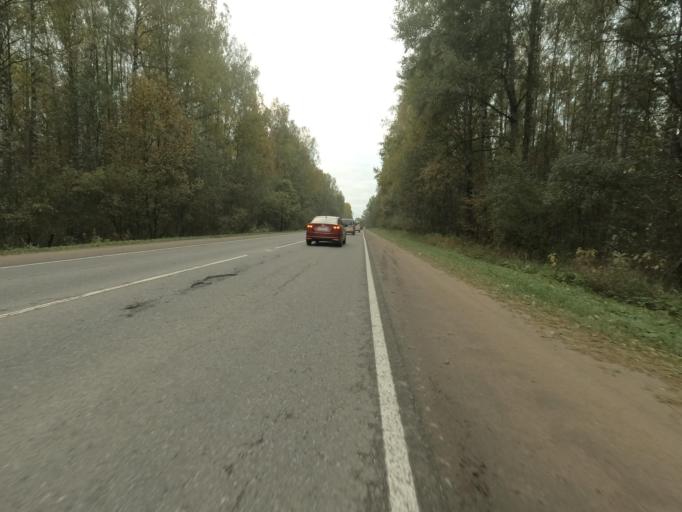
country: RU
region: Leningrad
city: Pavlovo
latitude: 59.8081
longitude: 30.9299
